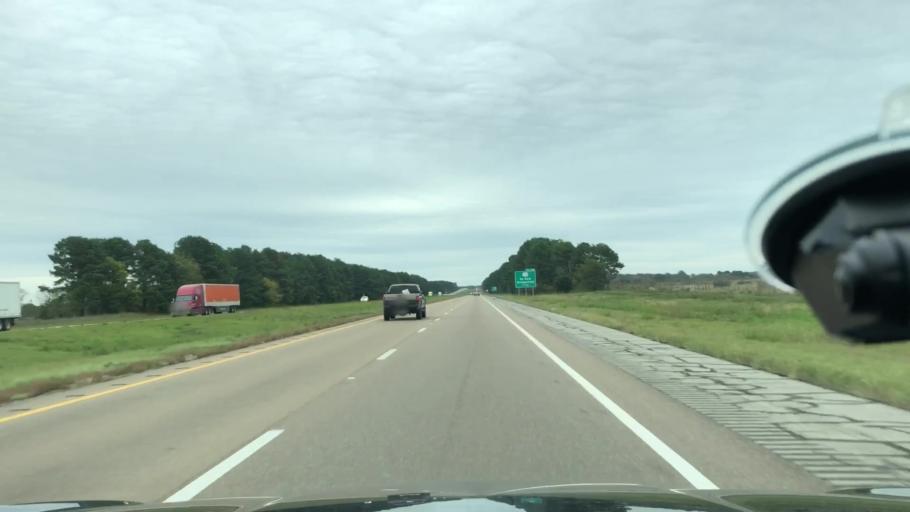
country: US
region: Texas
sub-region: Morris County
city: Omaha
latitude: 33.2911
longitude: -94.7669
